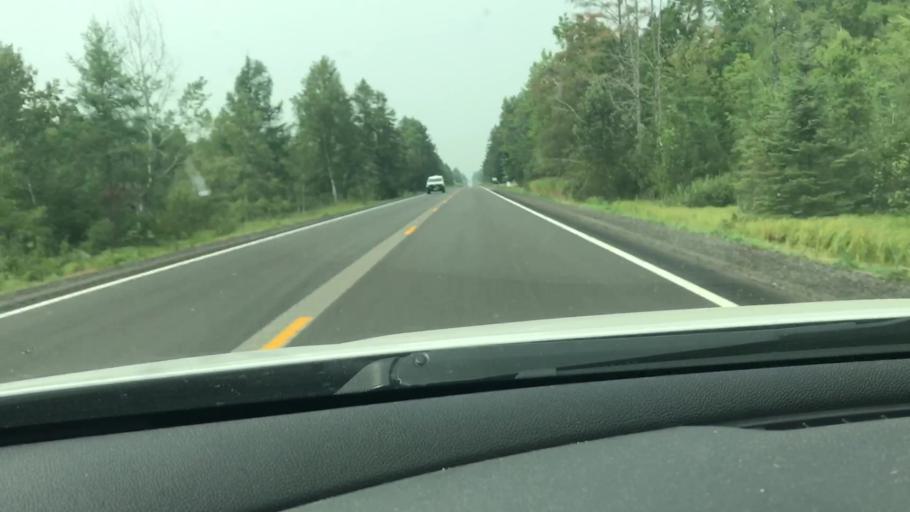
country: US
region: Minnesota
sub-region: Itasca County
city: Cohasset
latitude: 47.3490
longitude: -93.8344
